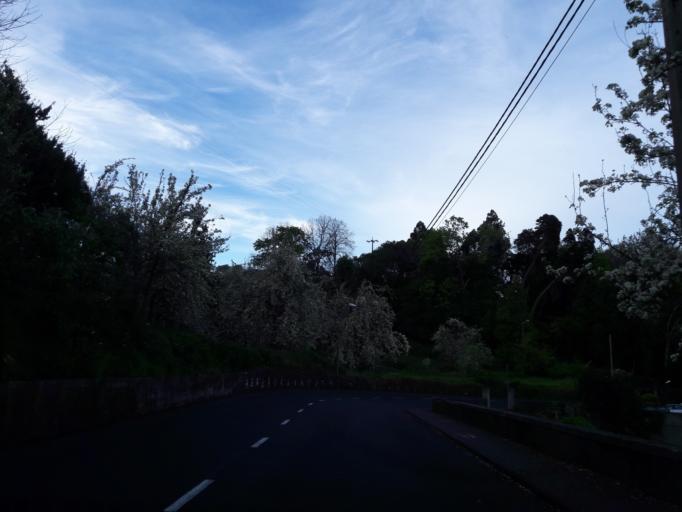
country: PT
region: Madeira
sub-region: Santa Cruz
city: Camacha
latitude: 32.6774
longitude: -16.8513
